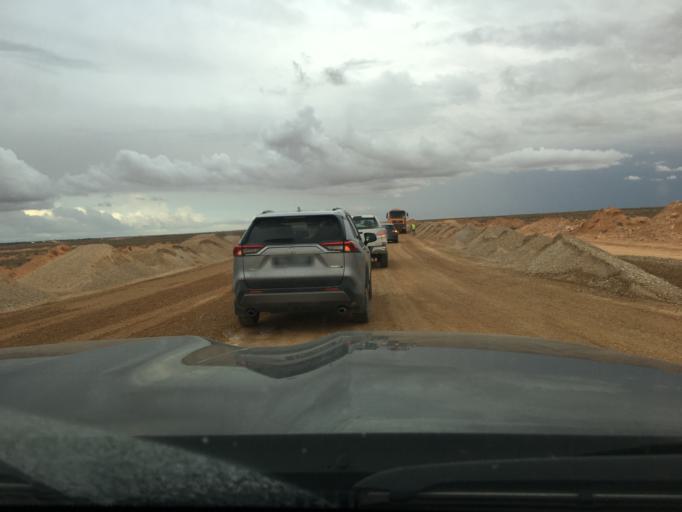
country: TN
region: Madanin
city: Medenine
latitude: 33.2663
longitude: 10.5827
